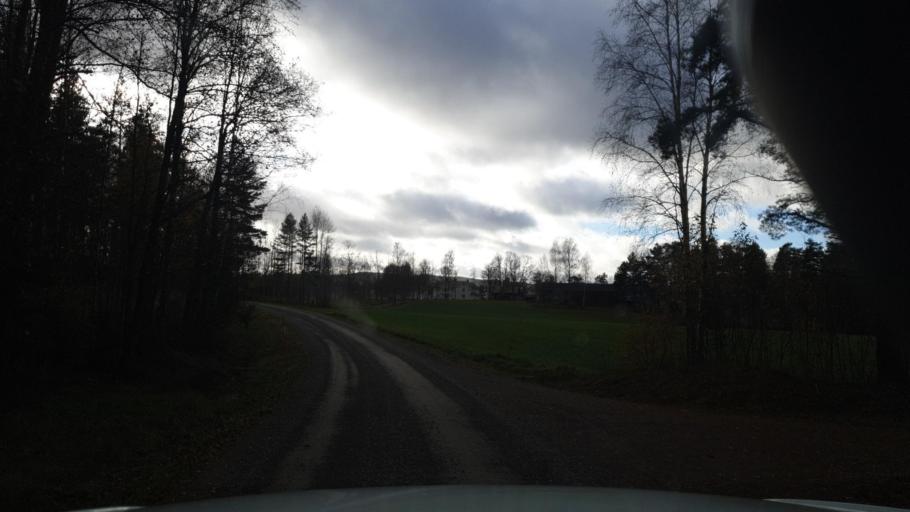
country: SE
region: Vaermland
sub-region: Arvika Kommun
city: Arvika
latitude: 59.4987
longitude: 12.7291
